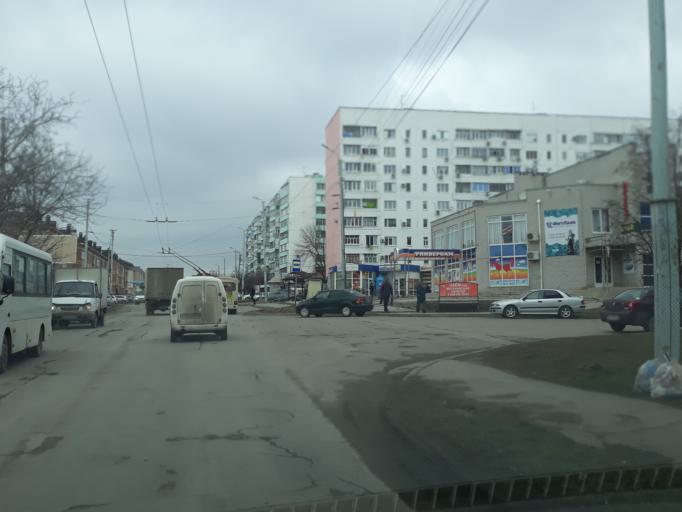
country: RU
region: Rostov
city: Taganrog
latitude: 47.2759
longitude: 38.9267
